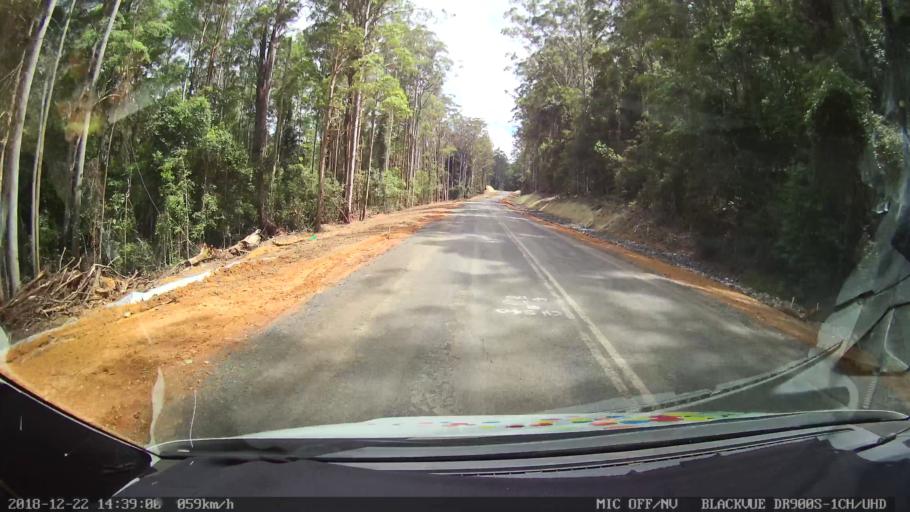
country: AU
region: New South Wales
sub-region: Bellingen
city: Dorrigo
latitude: -30.1428
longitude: 152.5946
